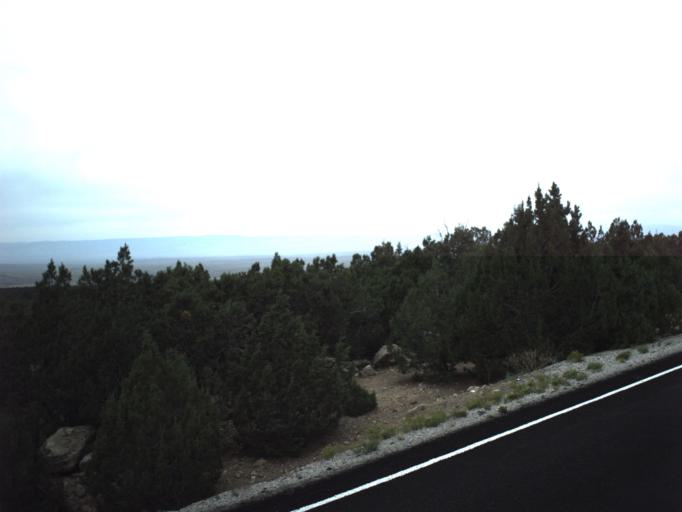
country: US
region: Utah
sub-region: Carbon County
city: East Carbon City
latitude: 39.4579
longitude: -110.3872
